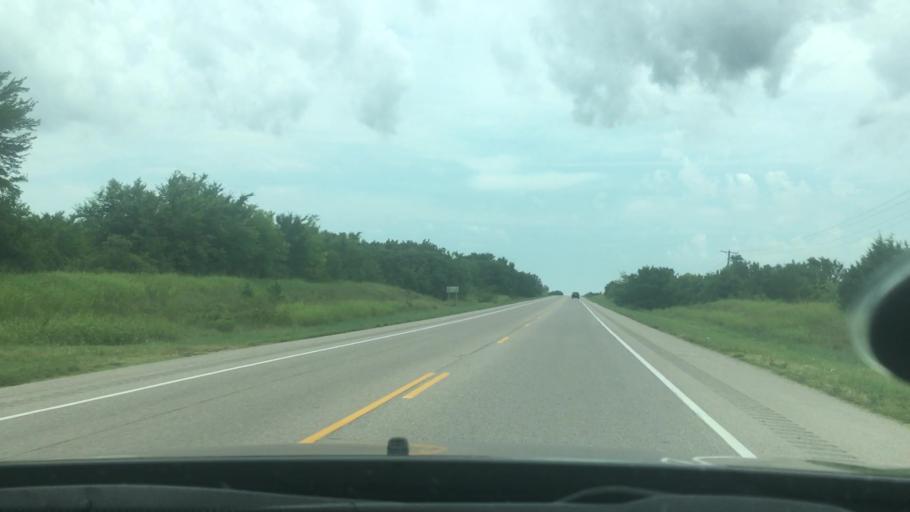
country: US
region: Oklahoma
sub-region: Seminole County
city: Konawa
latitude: 34.9715
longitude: -96.6789
